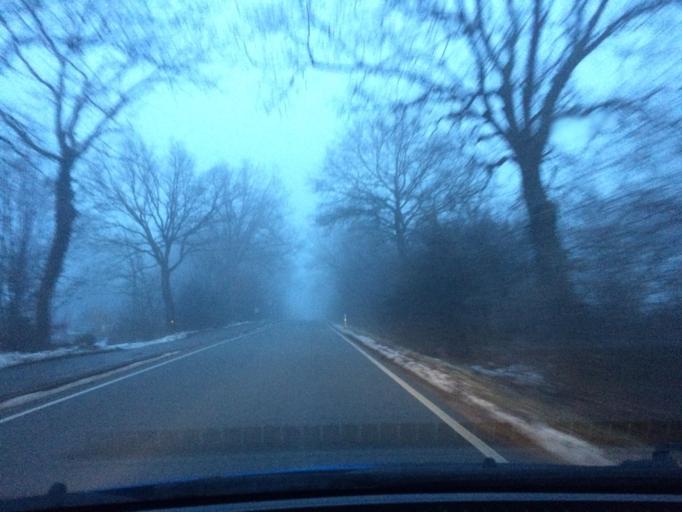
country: DE
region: Schleswig-Holstein
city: Kollow
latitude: 53.4791
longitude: 10.4646
